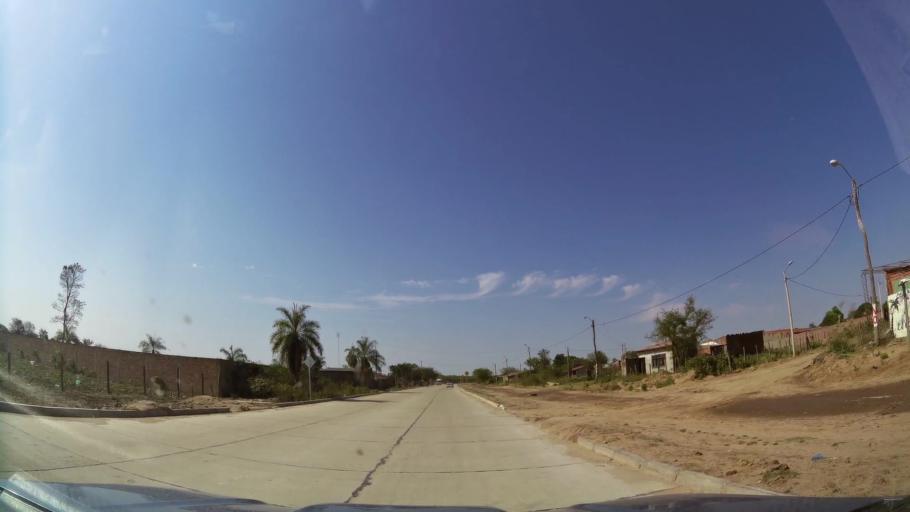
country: BO
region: Santa Cruz
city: Cotoca
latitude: -17.7140
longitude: -63.0678
